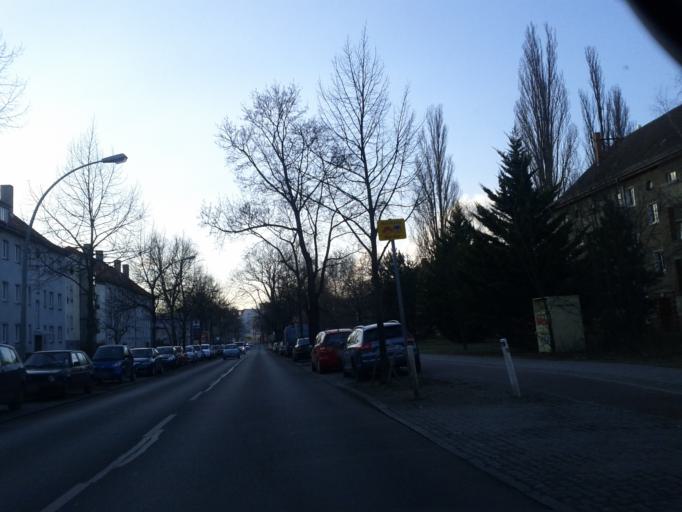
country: DE
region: Berlin
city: Kopenick Bezirk
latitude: 52.4520
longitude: 13.5806
